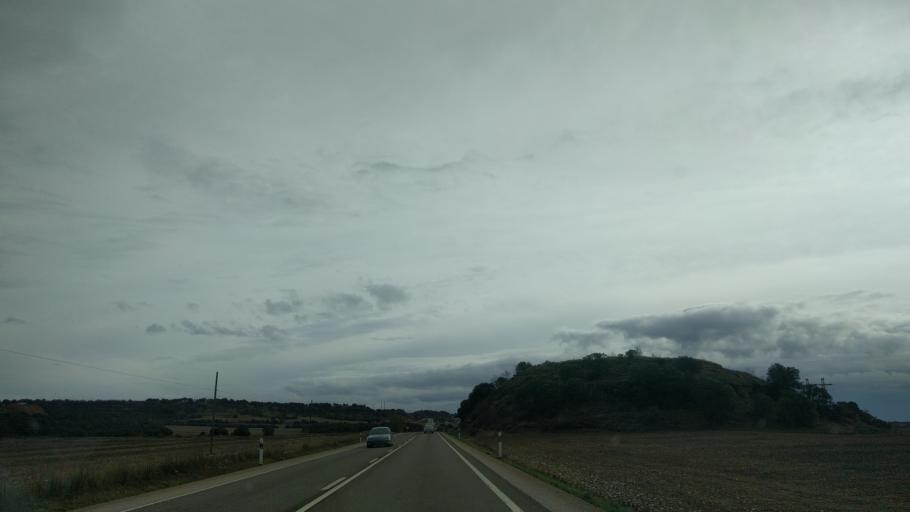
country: ES
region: Aragon
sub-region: Provincia de Huesca
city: Sietamo
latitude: 42.1317
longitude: -0.3058
